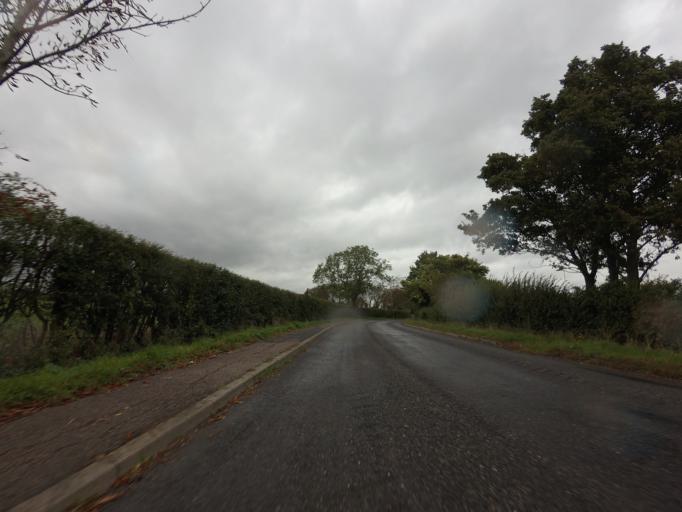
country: GB
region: England
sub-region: Cambridgeshire
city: Comberton
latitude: 52.1601
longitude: -0.0007
